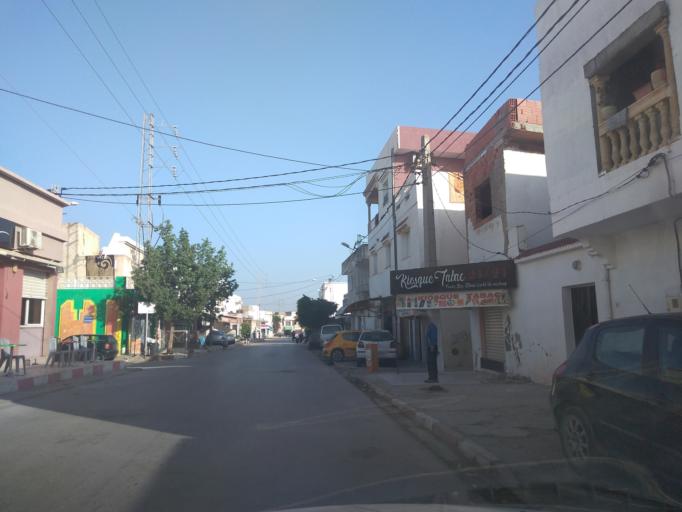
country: TN
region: Manouba
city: Manouba
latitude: 36.7908
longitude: 10.0887
